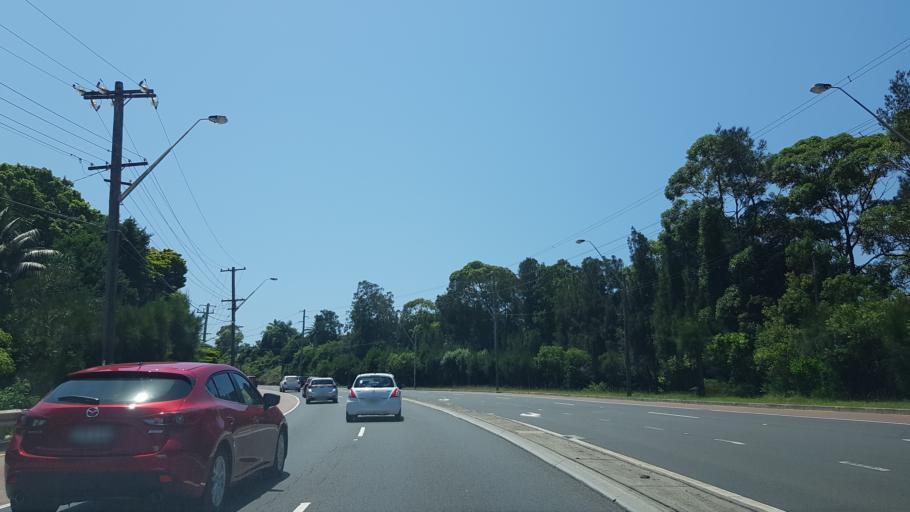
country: AU
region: New South Wales
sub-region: Pittwater
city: Warriewood
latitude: -33.6918
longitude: 151.3050
